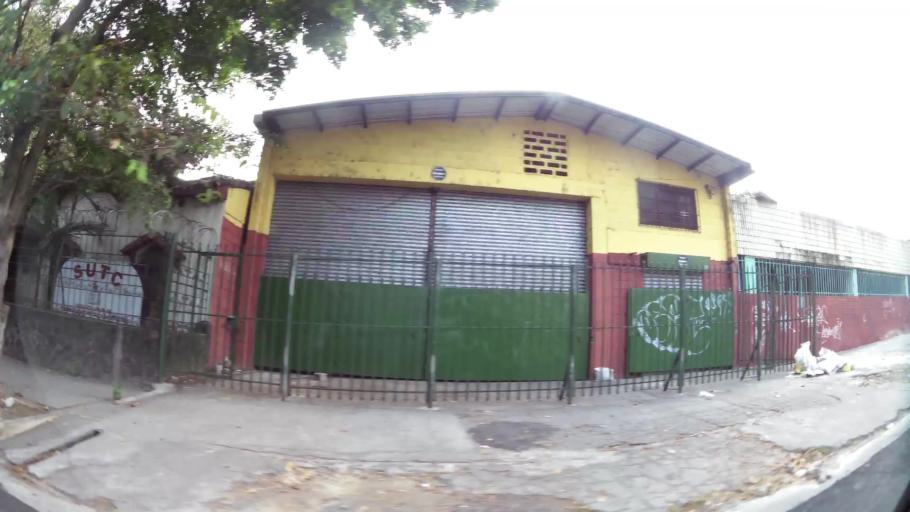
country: SV
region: San Salvador
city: San Salvador
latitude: 13.7060
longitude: -89.1907
